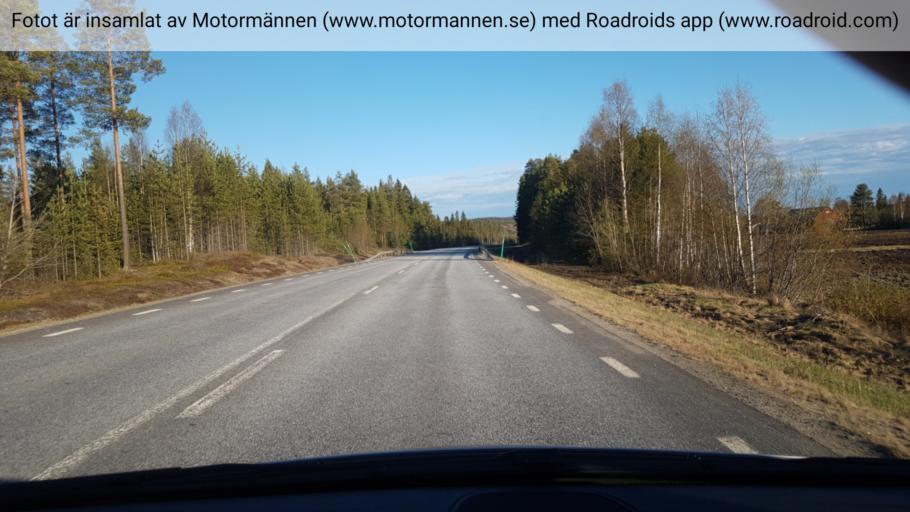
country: SE
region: Vaesterbotten
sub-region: Vannas Kommun
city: Vaennaes
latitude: 64.0056
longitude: 19.7177
